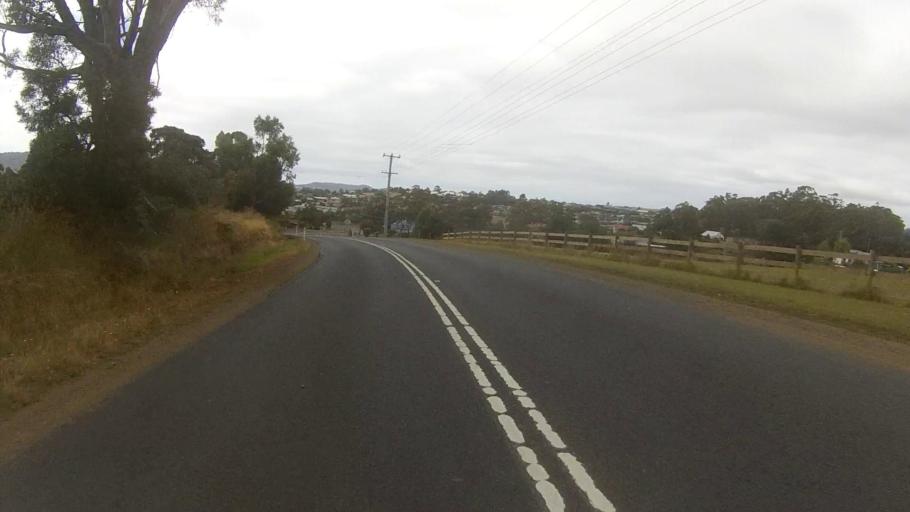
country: AU
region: Tasmania
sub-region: Kingborough
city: Margate
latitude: -43.0209
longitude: 147.2540
